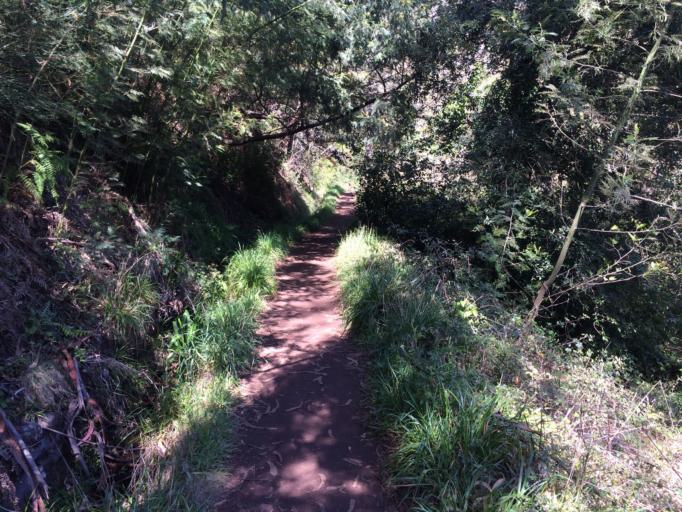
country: PT
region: Madeira
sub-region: Santa Cruz
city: Camacha
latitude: 32.6792
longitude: -16.8616
